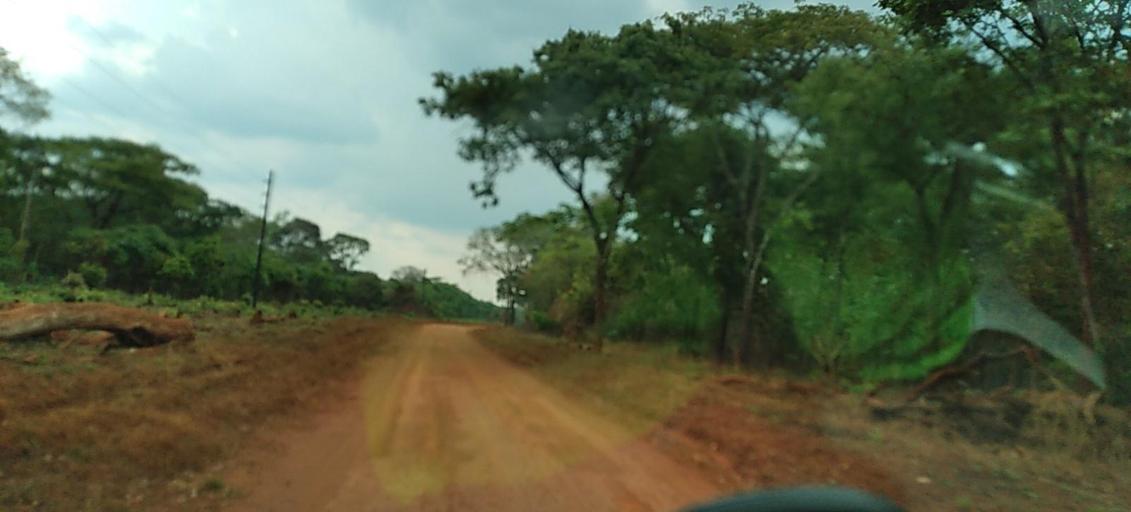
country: ZM
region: North-Western
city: Solwezi
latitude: -12.7811
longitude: 26.4866
